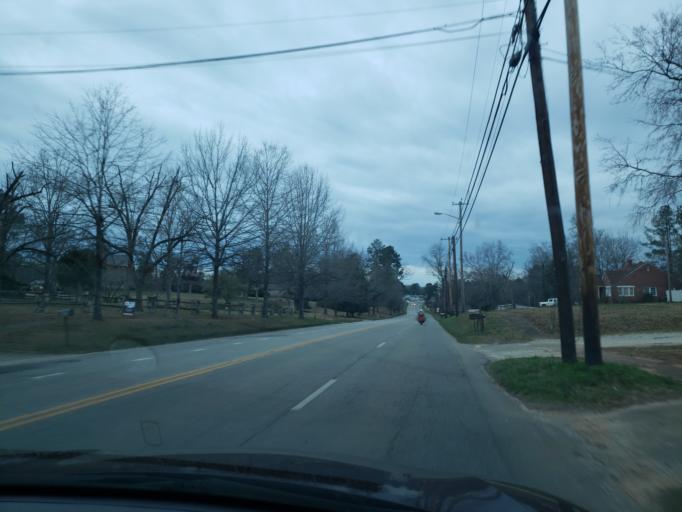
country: US
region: Alabama
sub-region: Chambers County
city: Lafayette
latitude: 32.9052
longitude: -85.4012
